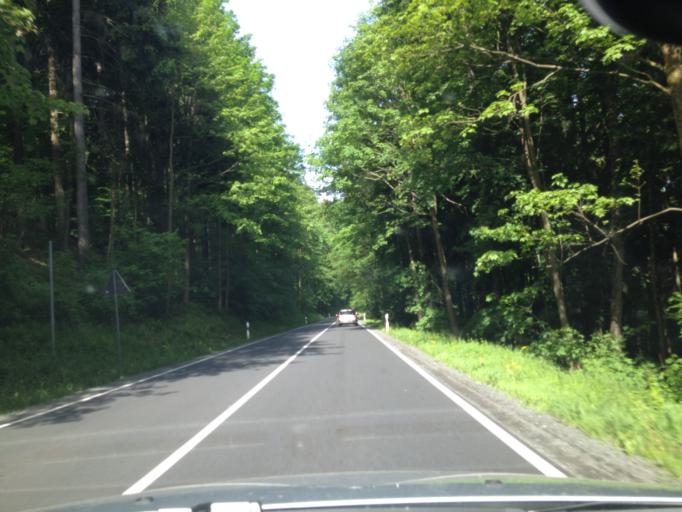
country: DE
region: Saxony
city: Thum
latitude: 50.6675
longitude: 12.9615
